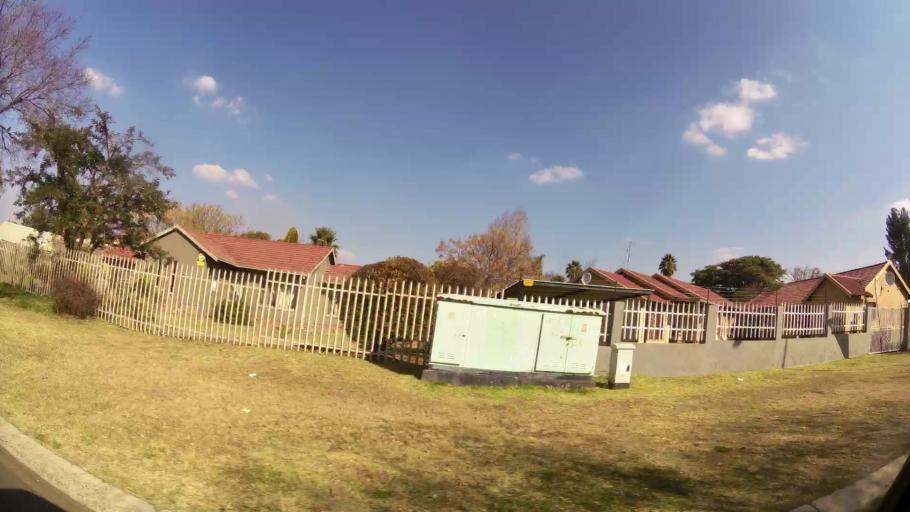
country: ZA
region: Gauteng
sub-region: Ekurhuleni Metropolitan Municipality
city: Boksburg
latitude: -26.2466
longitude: 28.3078
